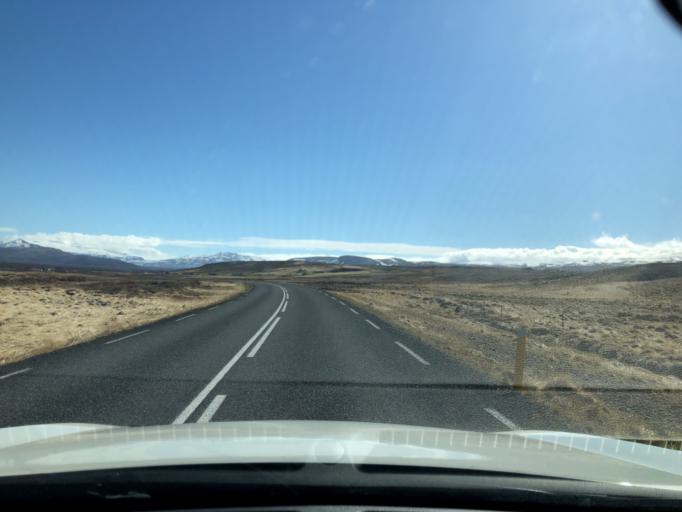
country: IS
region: South
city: Hveragerdi
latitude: 64.6990
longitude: -21.0683
